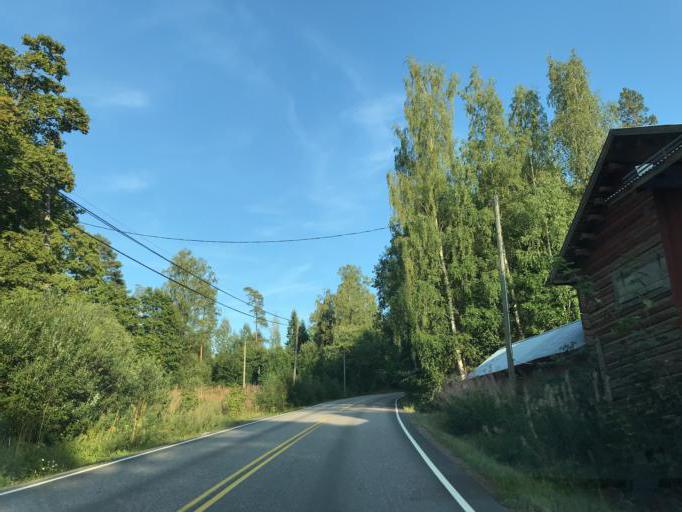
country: FI
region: Uusimaa
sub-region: Helsinki
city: Vihti
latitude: 60.4185
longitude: 24.3859
